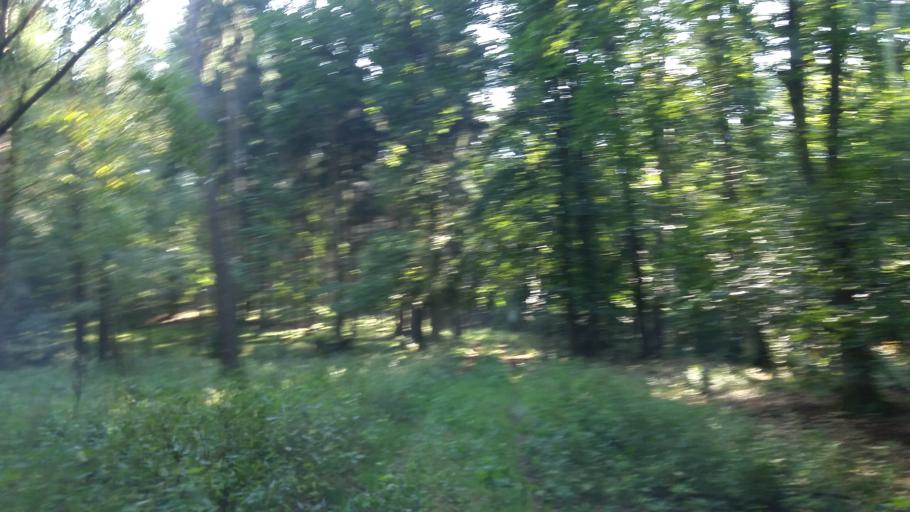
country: PL
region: West Pomeranian Voivodeship
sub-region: Powiat choszczenski
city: Pelczyce
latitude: 52.9724
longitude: 15.3530
